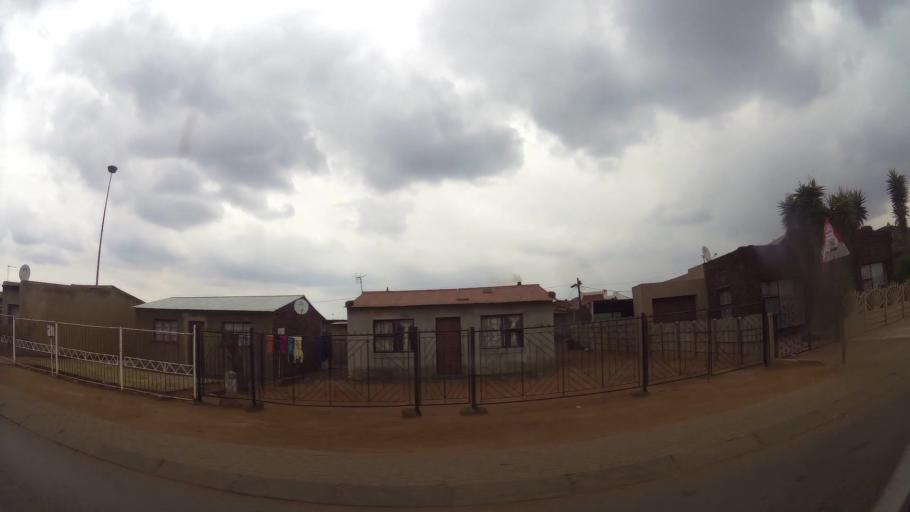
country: ZA
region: Gauteng
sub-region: Ekurhuleni Metropolitan Municipality
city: Germiston
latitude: -26.3457
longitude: 28.1498
